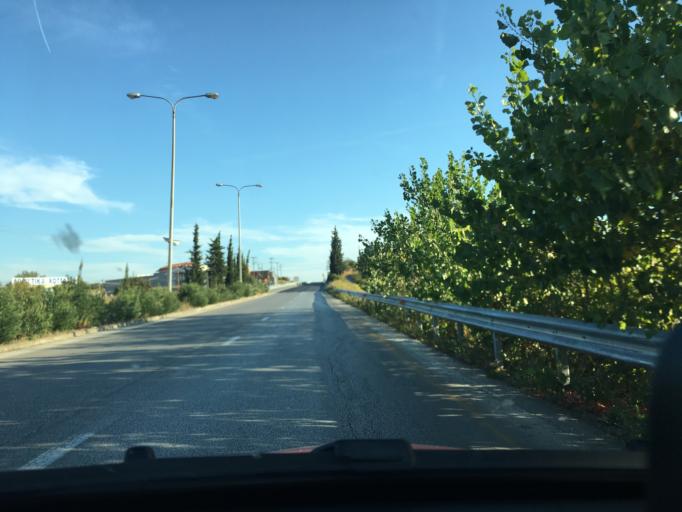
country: GR
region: Central Macedonia
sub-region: Nomos Chalkidikis
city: Nea Moudhania
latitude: 40.2407
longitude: 23.3007
